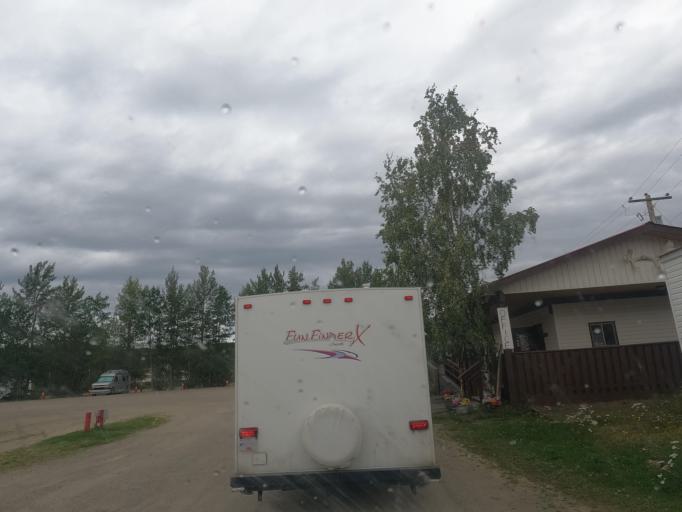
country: CA
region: Yukon
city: Watson Lake
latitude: 60.0635
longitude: -128.7065
